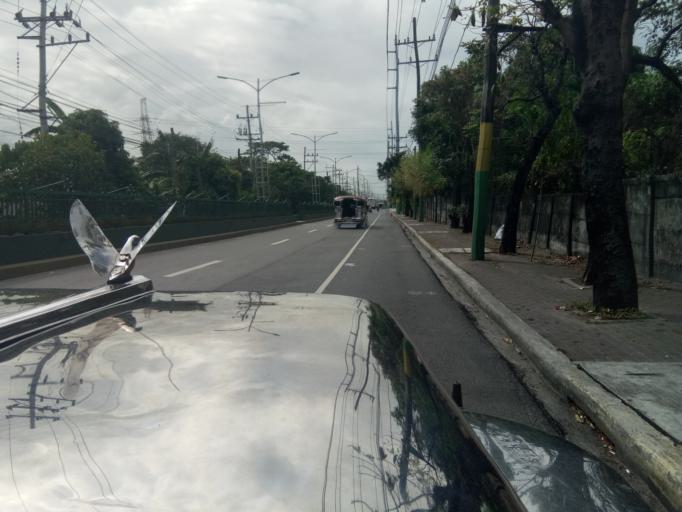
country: PH
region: Calabarzon
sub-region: Province of Cavite
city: Dasmarinas
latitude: 14.3086
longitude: 120.9516
